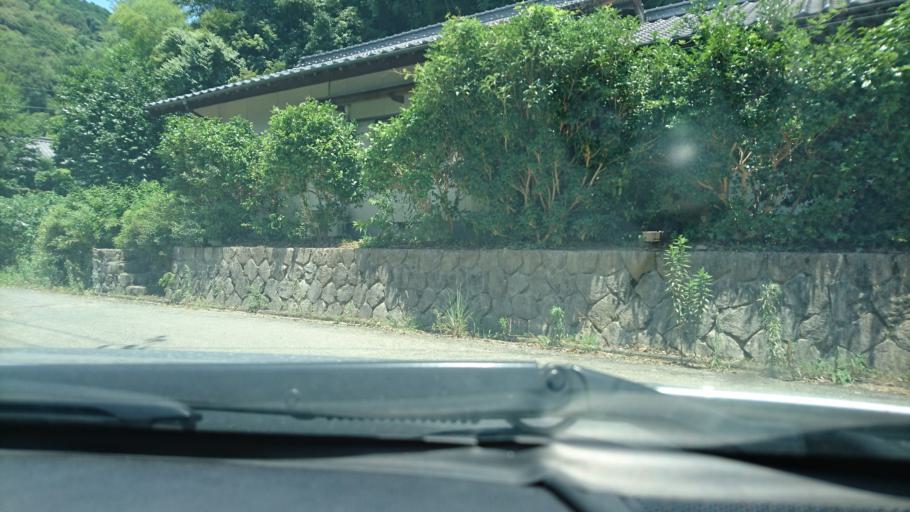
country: JP
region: Ehime
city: Ozu
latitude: 33.5102
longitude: 132.5303
